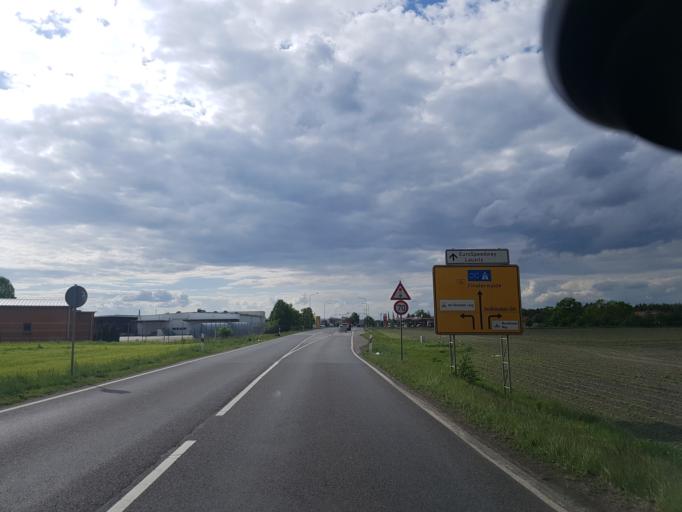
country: DE
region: Brandenburg
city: Grossraschen
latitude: 51.5790
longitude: 14.0349
